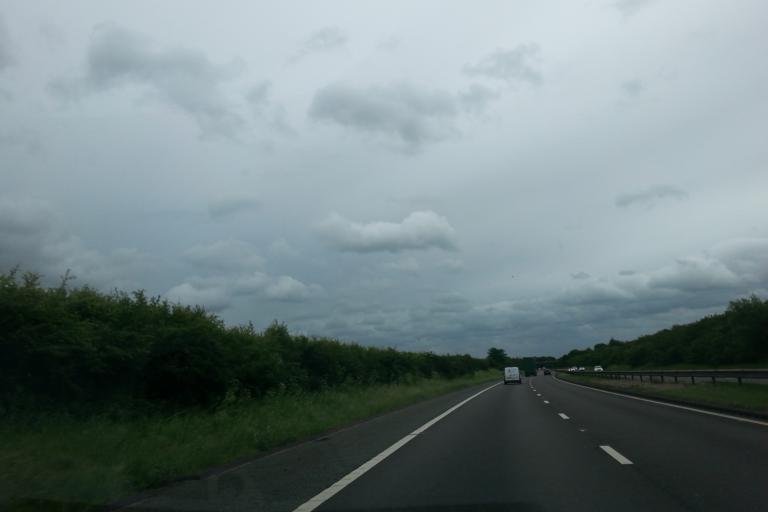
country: GB
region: England
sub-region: Doncaster
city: Tickhill
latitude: 53.4423
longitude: -1.1033
